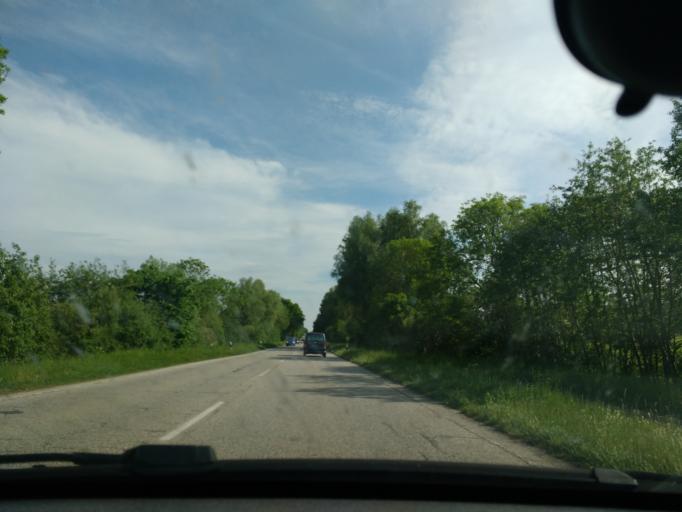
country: DE
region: Schleswig-Holstein
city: Pogeez
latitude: 53.7400
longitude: 10.7322
